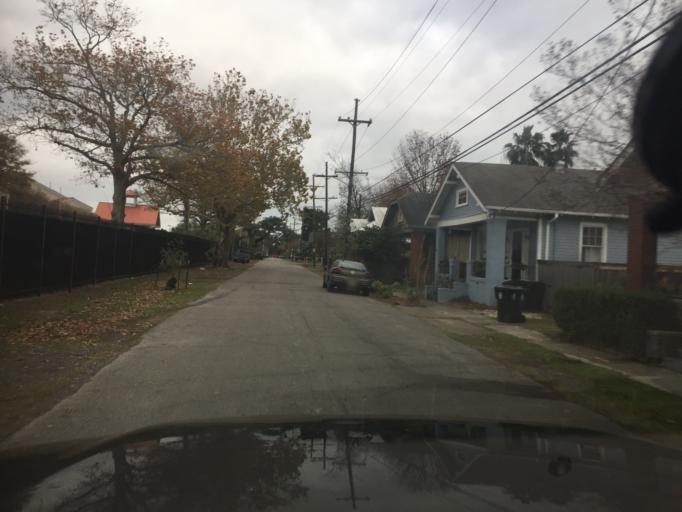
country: US
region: Louisiana
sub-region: Orleans Parish
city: New Orleans
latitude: 29.9815
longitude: -90.0807
